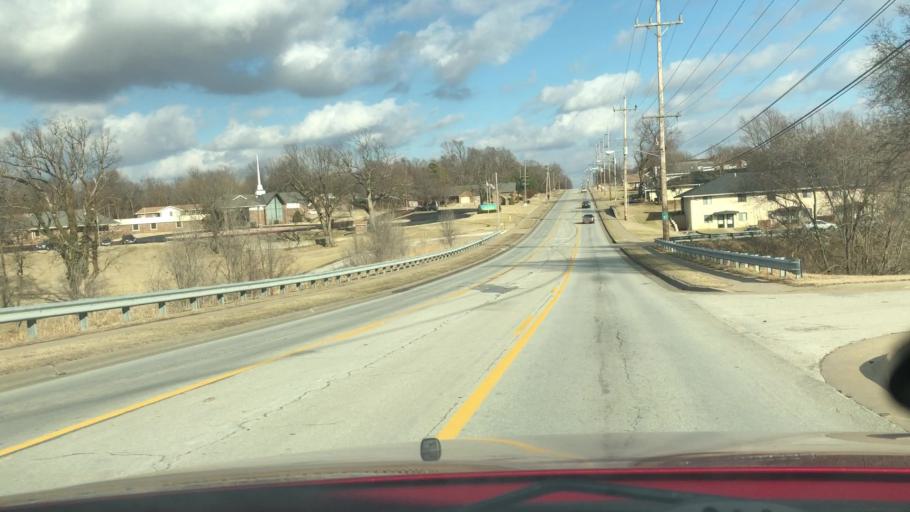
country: US
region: Missouri
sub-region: Greene County
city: Springfield
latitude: 37.2516
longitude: -93.2927
